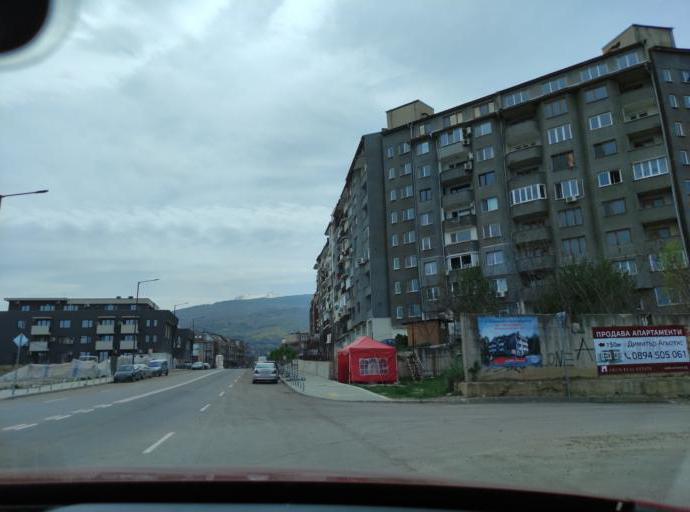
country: BG
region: Sofia-Capital
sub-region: Stolichna Obshtina
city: Sofia
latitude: 42.6380
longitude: 23.3418
